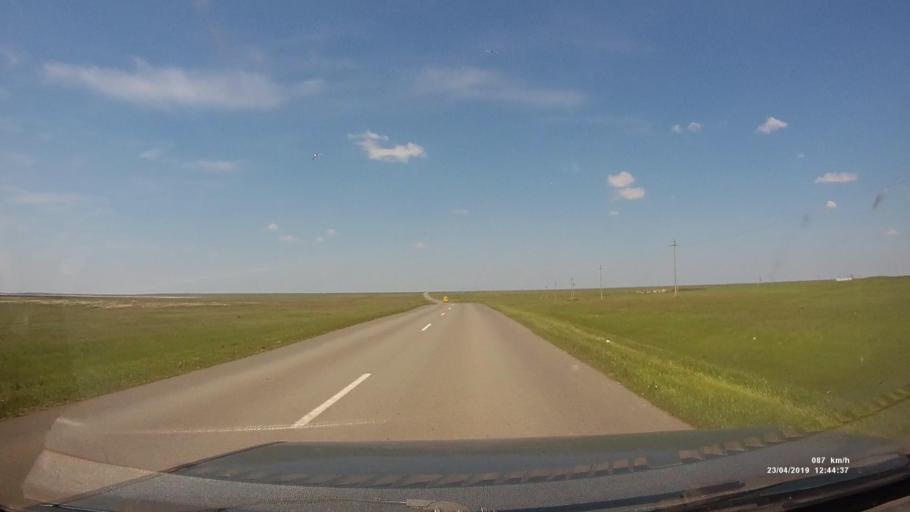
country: RU
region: Kalmykiya
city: Yashalta
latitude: 46.4792
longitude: 42.6466
